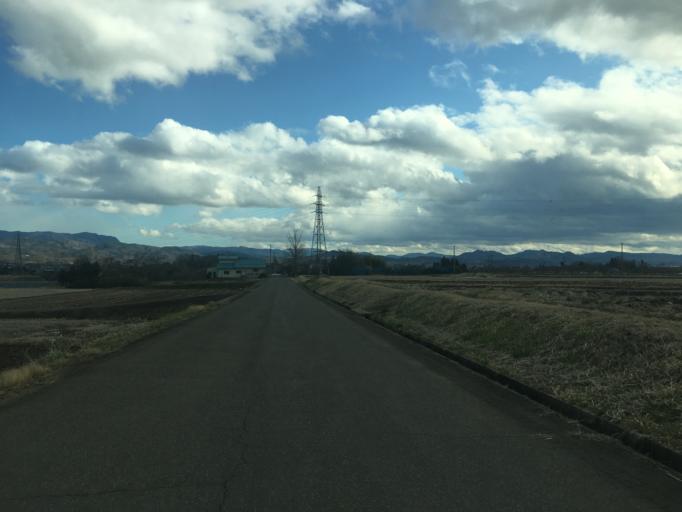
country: JP
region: Fukushima
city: Yanagawamachi-saiwaicho
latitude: 37.8811
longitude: 140.5867
